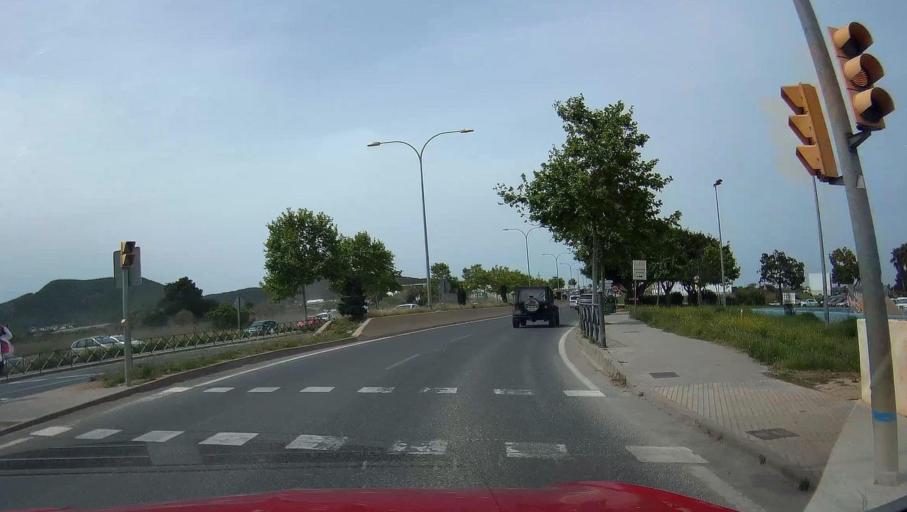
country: ES
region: Balearic Islands
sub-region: Illes Balears
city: Ibiza
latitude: 38.9162
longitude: 1.4283
